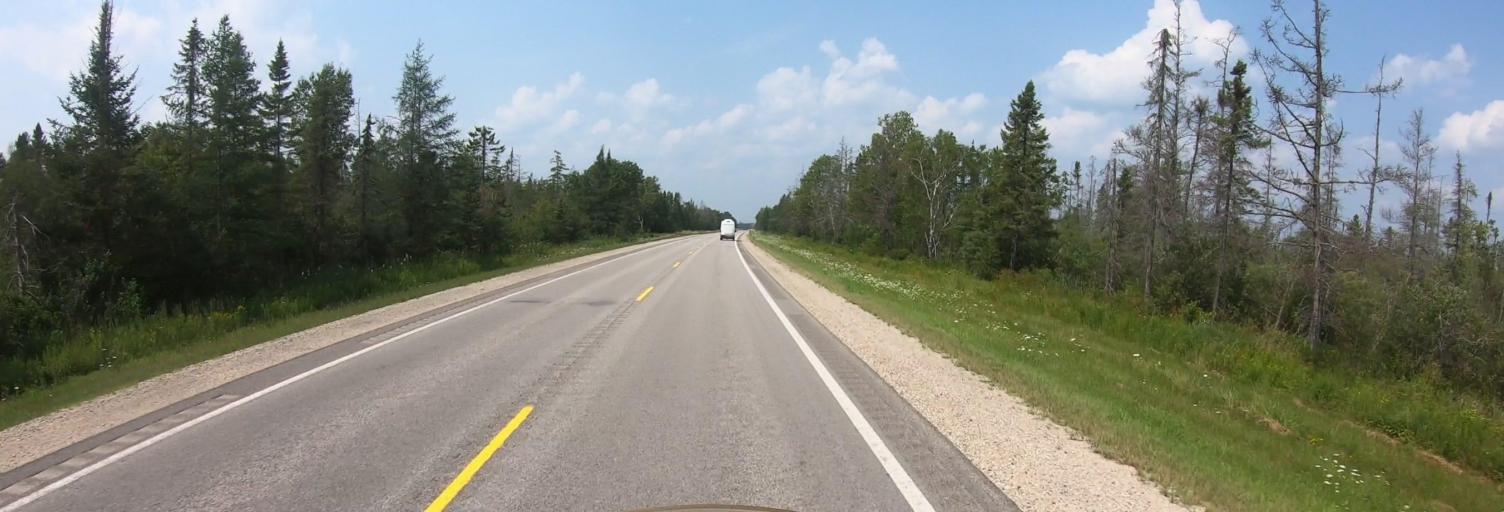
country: US
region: Michigan
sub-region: Luce County
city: Newberry
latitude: 46.3357
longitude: -85.8526
